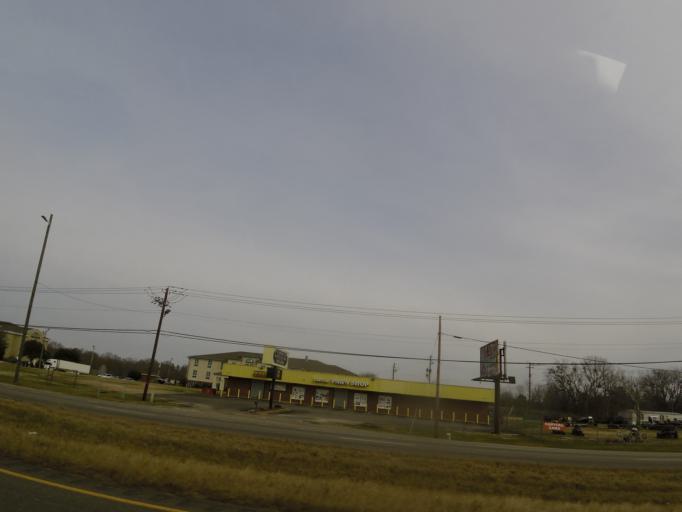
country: US
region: Alabama
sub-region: Montgomery County
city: Montgomery
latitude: 32.3145
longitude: -86.2274
